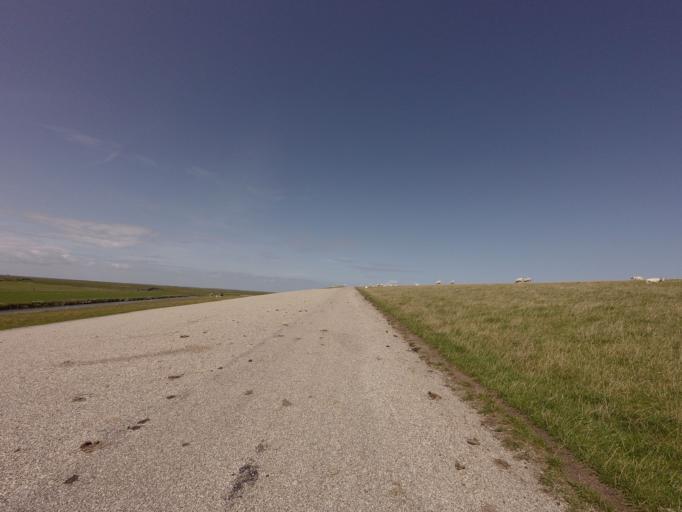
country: NL
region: Friesland
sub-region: Gemeente Dongeradeel
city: Holwerd
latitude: 53.3687
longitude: 5.8593
